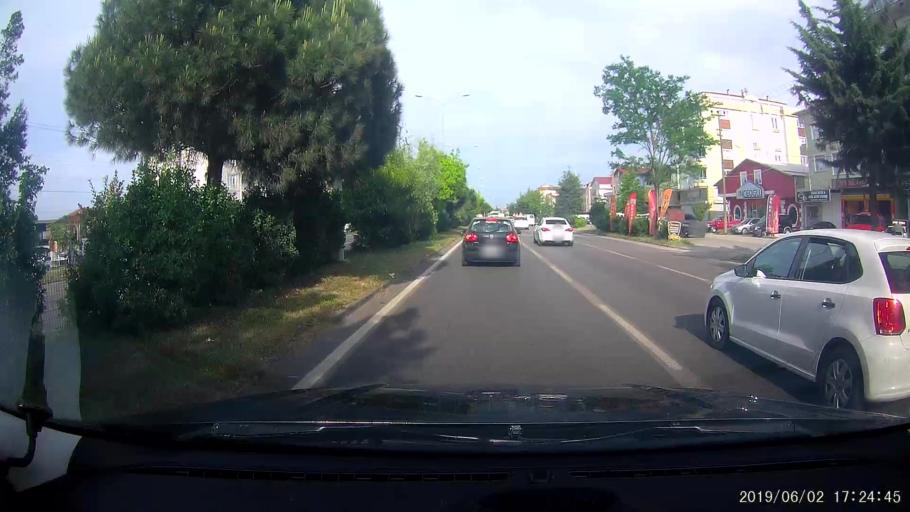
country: TR
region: Samsun
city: Carsamba
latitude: 41.2052
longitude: 36.7066
